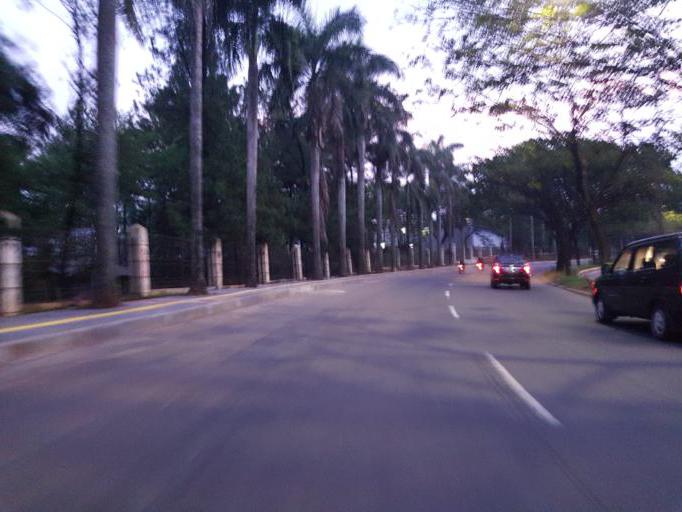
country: ID
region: West Java
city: Serpong
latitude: -6.3299
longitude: 106.6807
